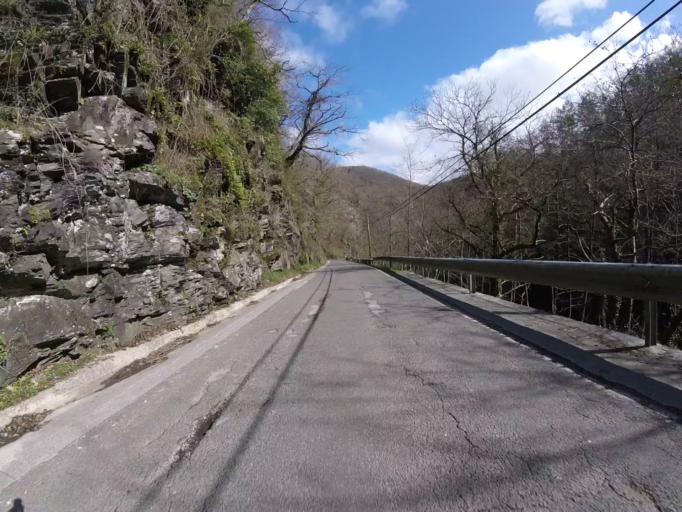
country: ES
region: Navarre
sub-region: Provincia de Navarra
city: Goizueta
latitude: 43.1389
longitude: -1.8482
